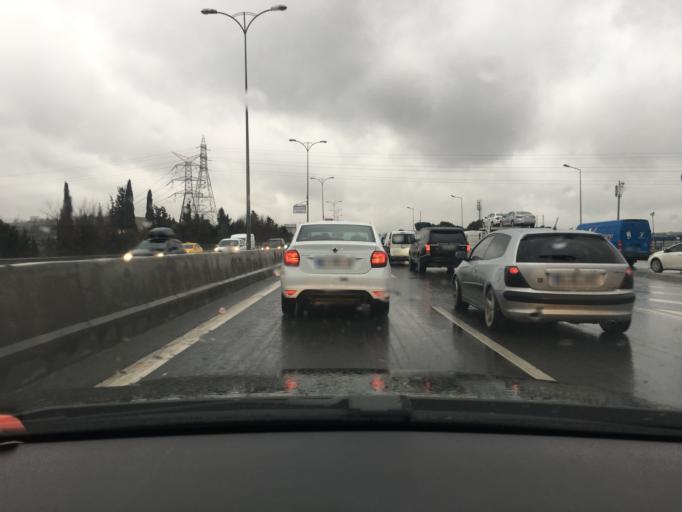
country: TR
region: Istanbul
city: Esenler
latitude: 41.0497
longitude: 28.8852
